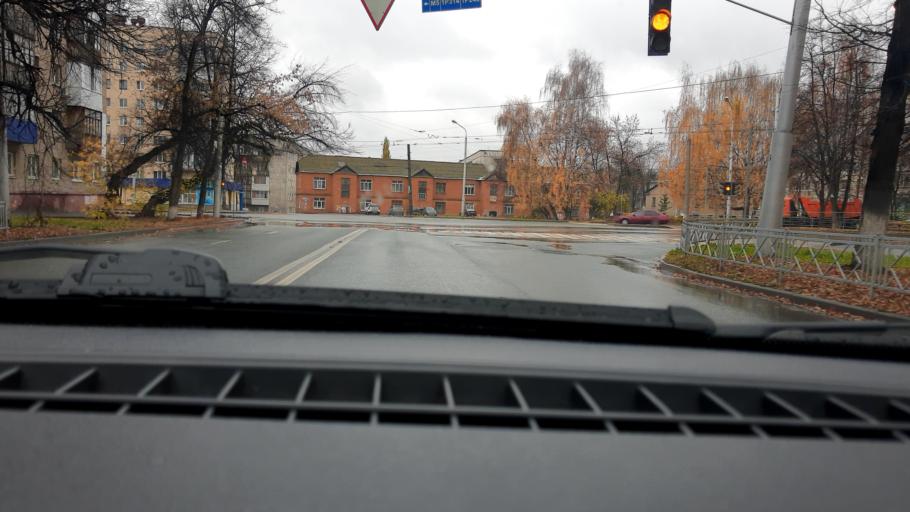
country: RU
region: Bashkortostan
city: Ufa
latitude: 54.8155
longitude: 56.1046
